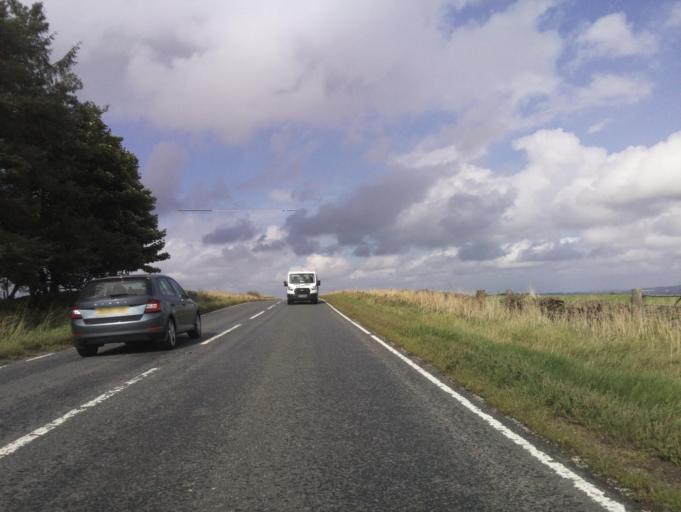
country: GB
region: England
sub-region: County Durham
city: Tow Law
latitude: 54.7713
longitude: -1.8515
